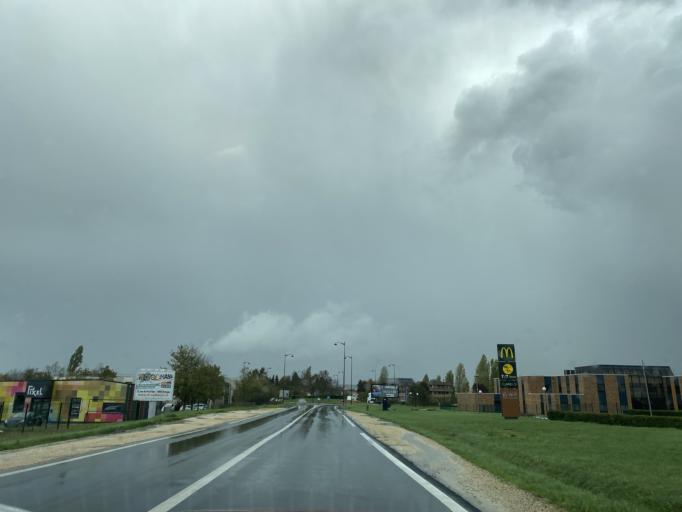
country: FR
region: Centre
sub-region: Departement du Cher
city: La Chapelle-Saint-Ursin
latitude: 47.0607
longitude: 2.3634
